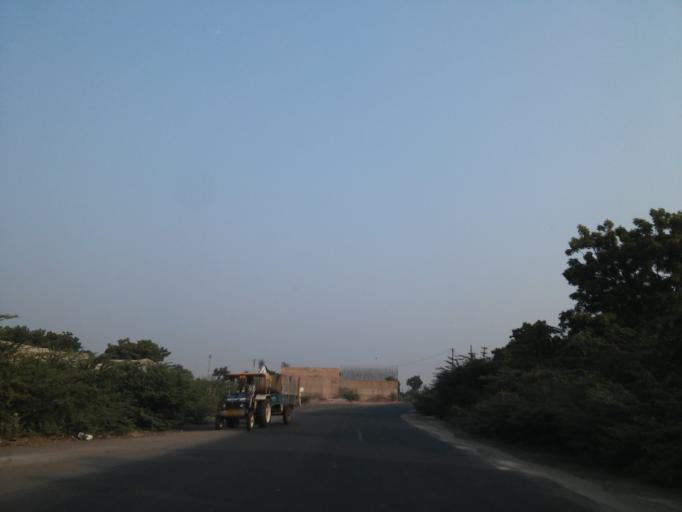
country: IN
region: Gujarat
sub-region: Kachchh
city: Bhachau
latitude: 23.3075
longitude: 70.3574
